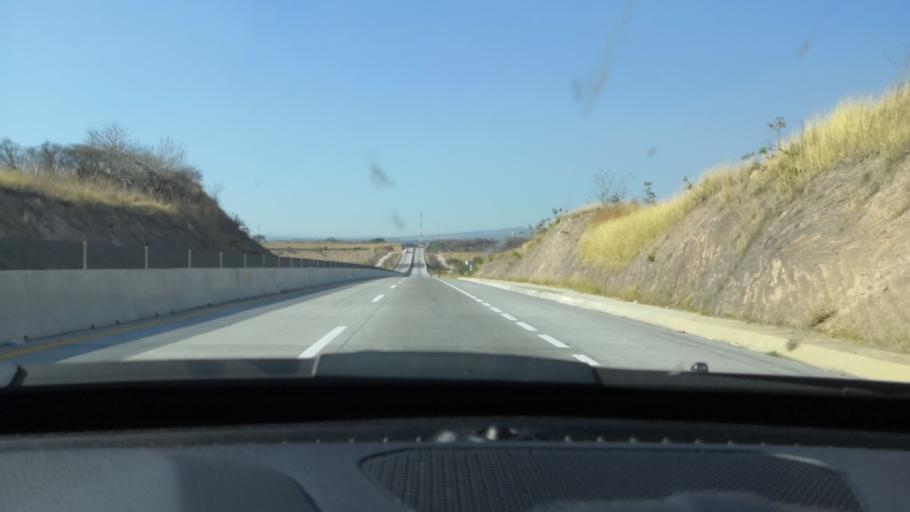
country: MX
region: Jalisco
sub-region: Zapotlanejo
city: La Mezquitera
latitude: 20.5943
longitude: -103.1002
